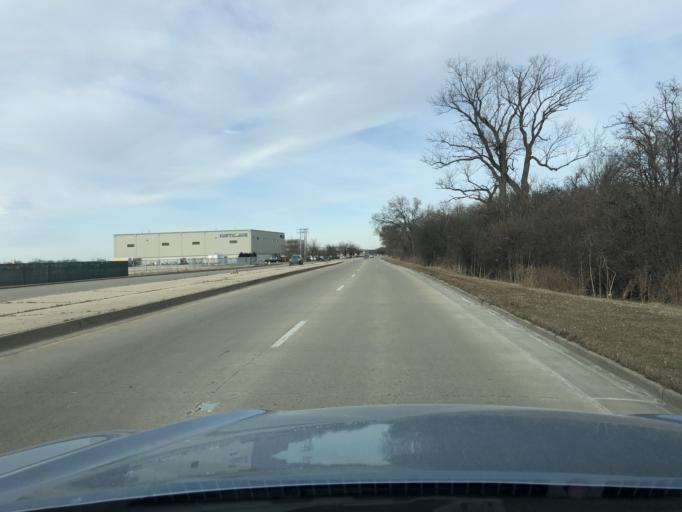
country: US
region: Illinois
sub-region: Cook County
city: Wheeling
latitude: 42.1108
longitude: -87.8911
